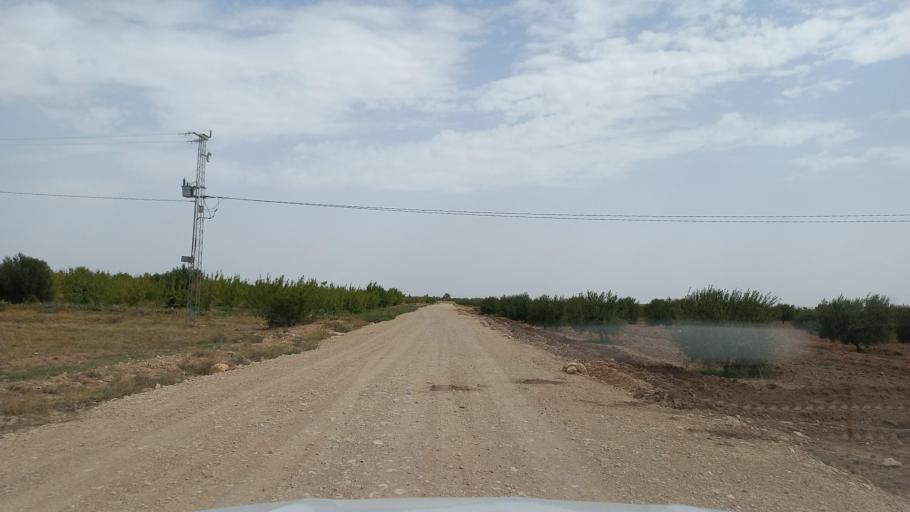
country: TN
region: Al Qasrayn
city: Kasserine
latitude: 35.2782
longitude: 9.0179
